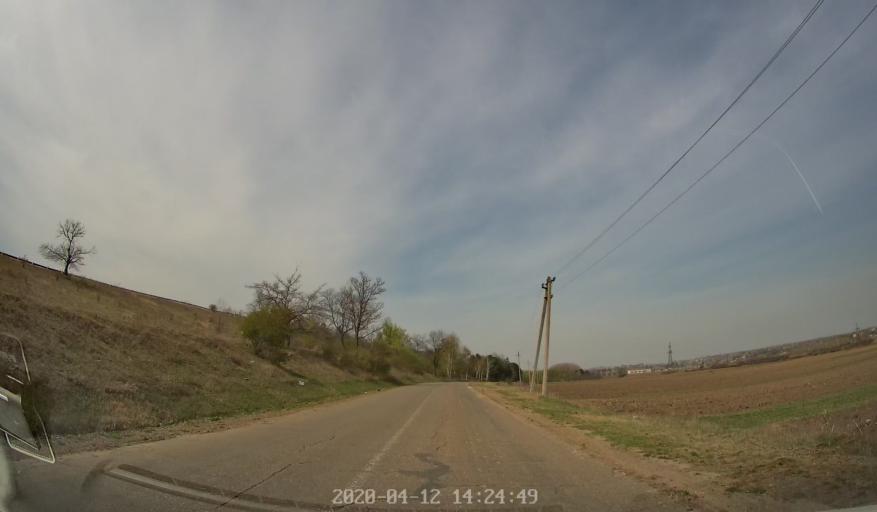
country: MD
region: Telenesti
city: Dubasari
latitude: 47.2653
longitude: 29.1267
